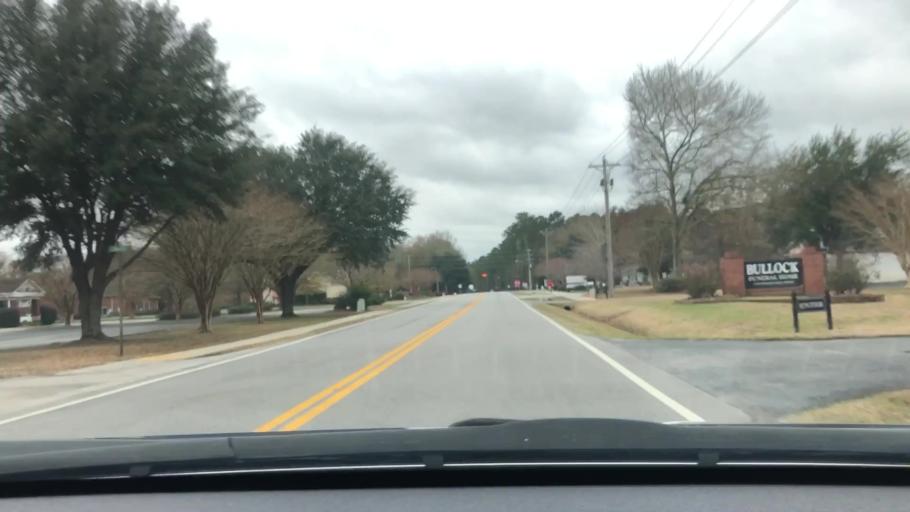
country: US
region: South Carolina
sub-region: Sumter County
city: Cherryvale
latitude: 33.9542
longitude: -80.4000
